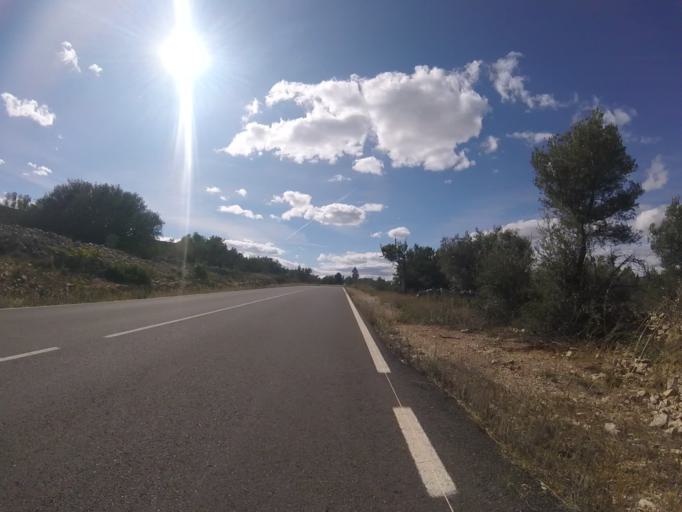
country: ES
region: Valencia
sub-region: Provincia de Castello
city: Cati
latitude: 40.4309
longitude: 0.0937
